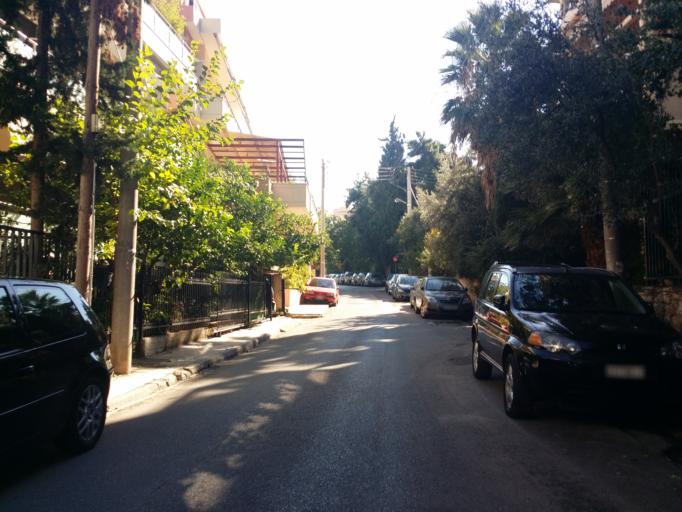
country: GR
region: Attica
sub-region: Nomarchia Athinas
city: Agia Paraskevi
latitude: 38.0180
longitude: 23.8359
